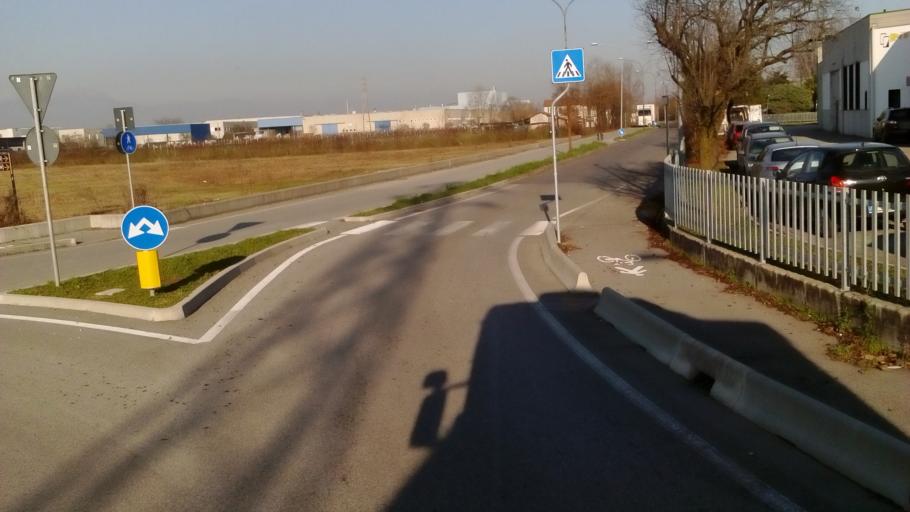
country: IT
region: Veneto
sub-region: Provincia di Treviso
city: Oderzo
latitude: 45.8031
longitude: 12.4995
